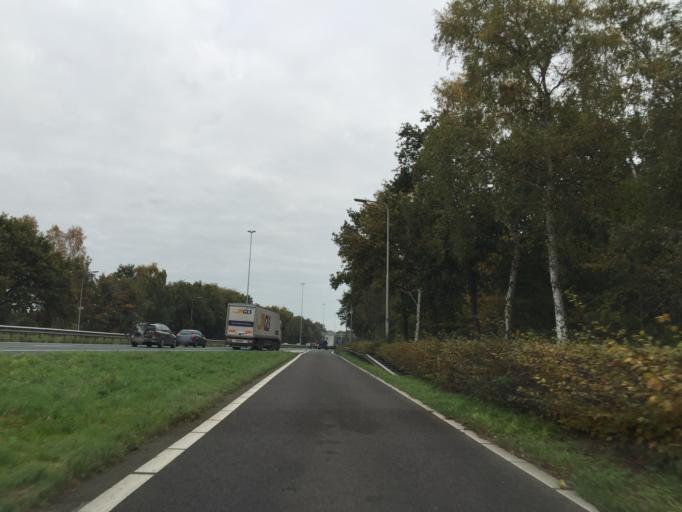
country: NL
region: North Brabant
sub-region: Gemeente Oosterhout
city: Oosterhout
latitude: 51.6321
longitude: 4.8773
